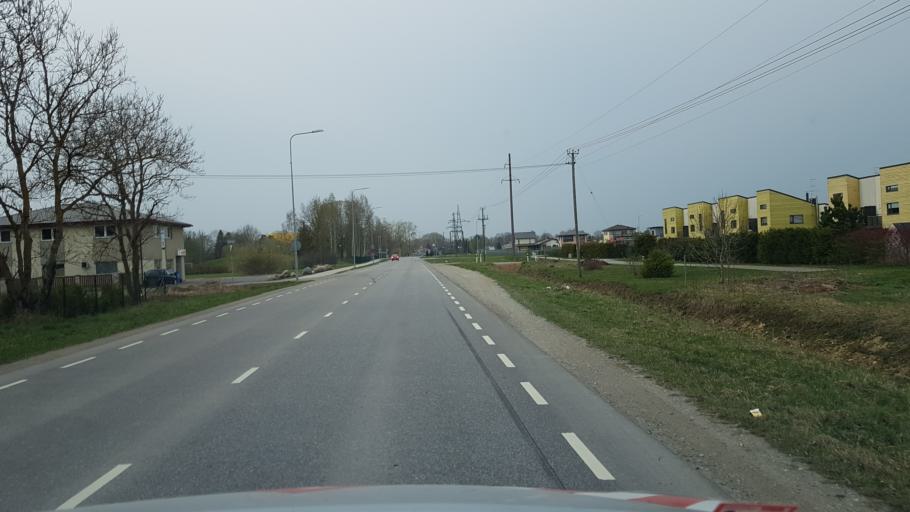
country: EE
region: Harju
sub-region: Joelaehtme vald
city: Loo
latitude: 59.4012
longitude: 24.9489
